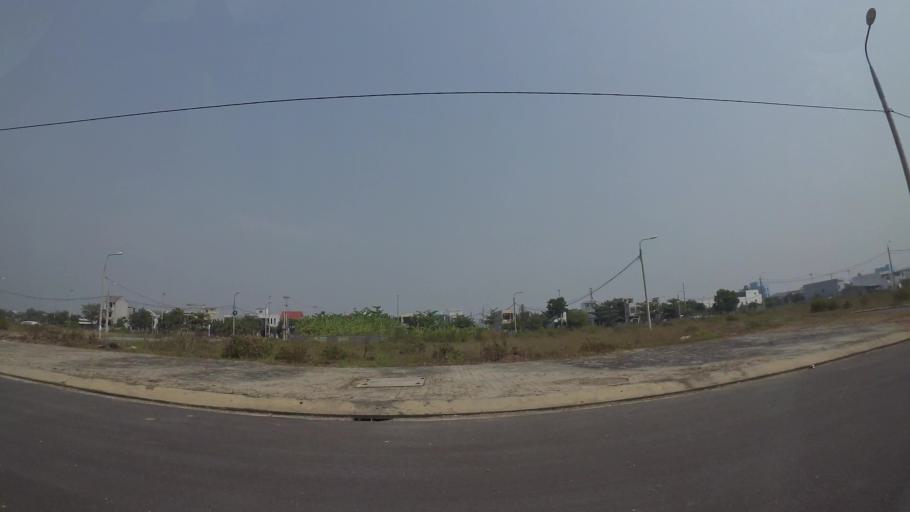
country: VN
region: Da Nang
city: Cam Le
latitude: 15.9739
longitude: 108.2134
